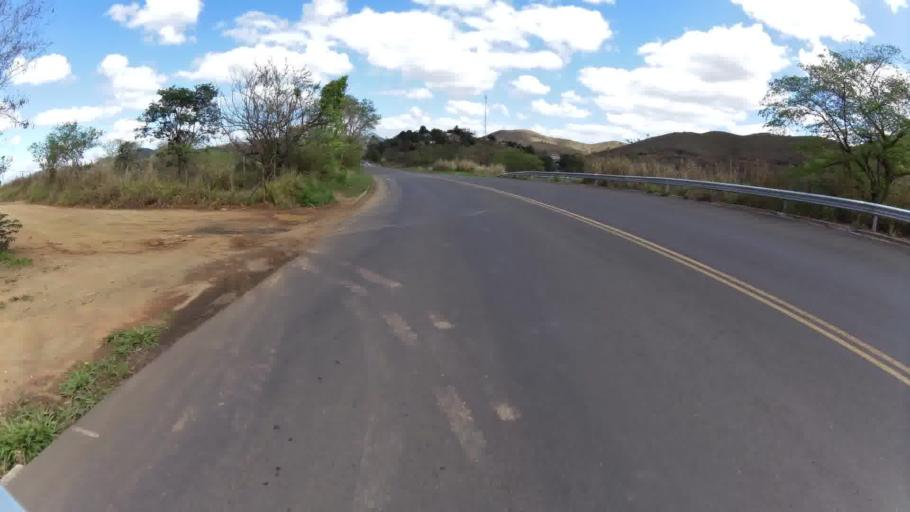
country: BR
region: Rio de Janeiro
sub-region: Itaperuna
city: Itaperuna
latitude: -21.2714
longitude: -41.7820
